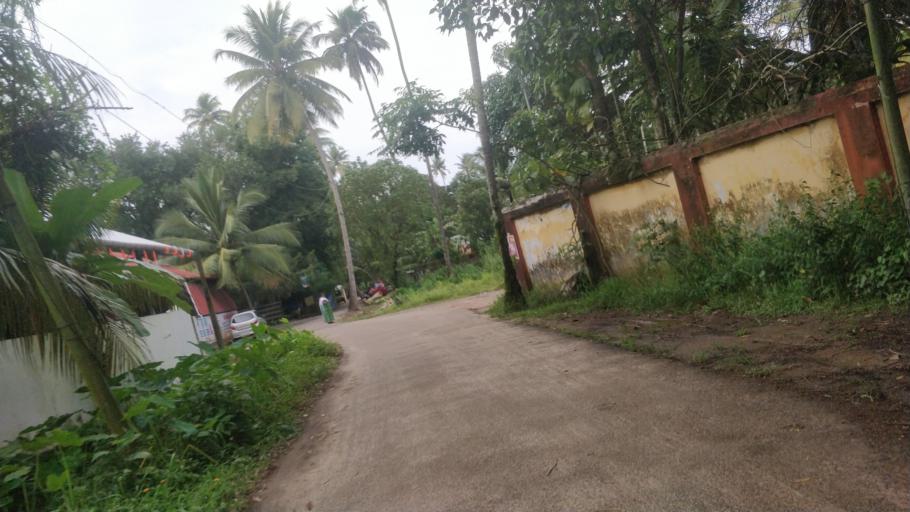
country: IN
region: Kerala
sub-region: Alappuzha
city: Shertallai
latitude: 9.6970
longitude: 76.3613
